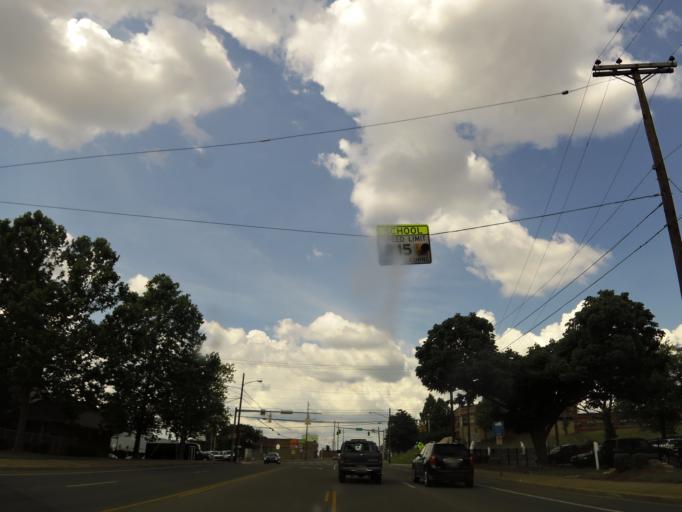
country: US
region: Tennessee
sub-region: Davidson County
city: Nashville
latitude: 36.1420
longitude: -86.7872
